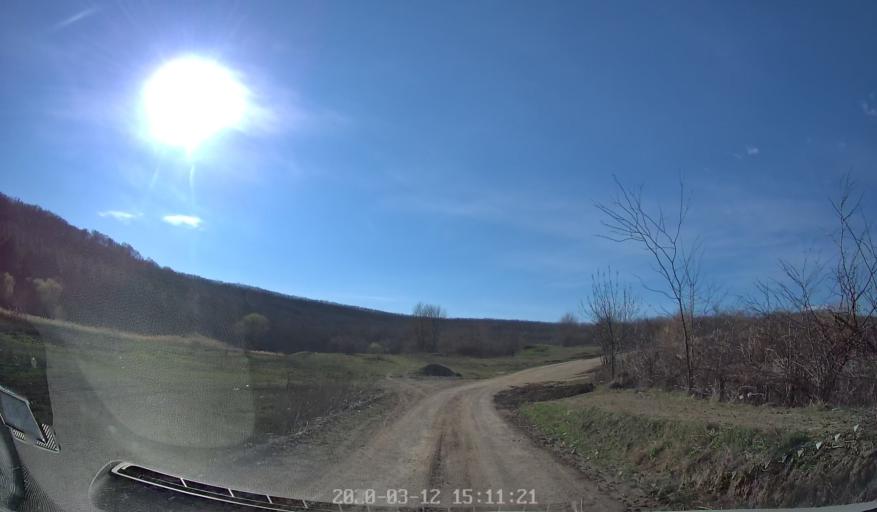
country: MD
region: Chisinau
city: Ciorescu
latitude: 47.2268
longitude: 28.9764
